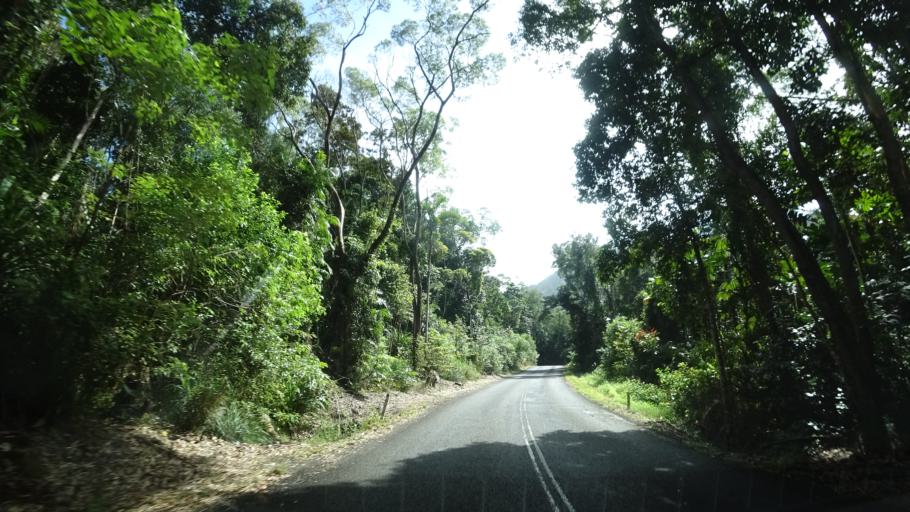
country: AU
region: Queensland
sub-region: Cairns
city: Port Douglas
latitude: -16.2588
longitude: 145.4208
